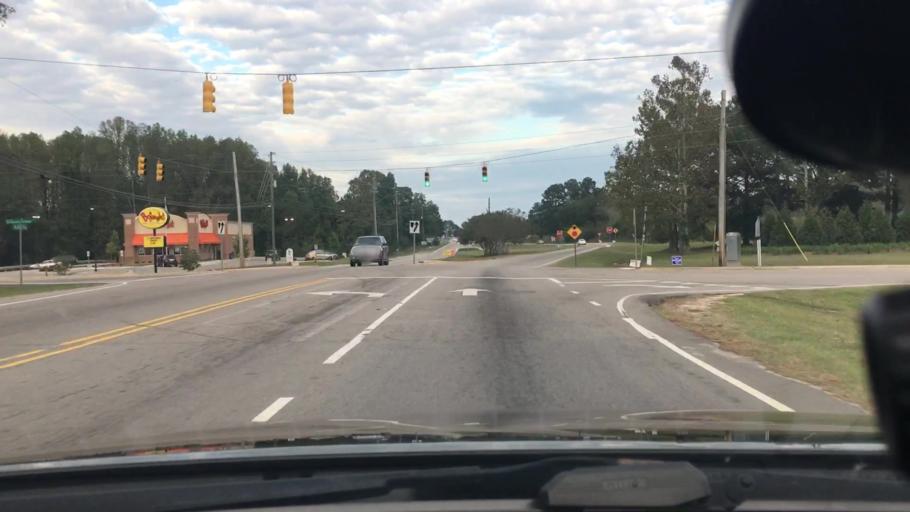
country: US
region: North Carolina
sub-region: Moore County
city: Carthage
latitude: 35.3413
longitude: -79.4006
